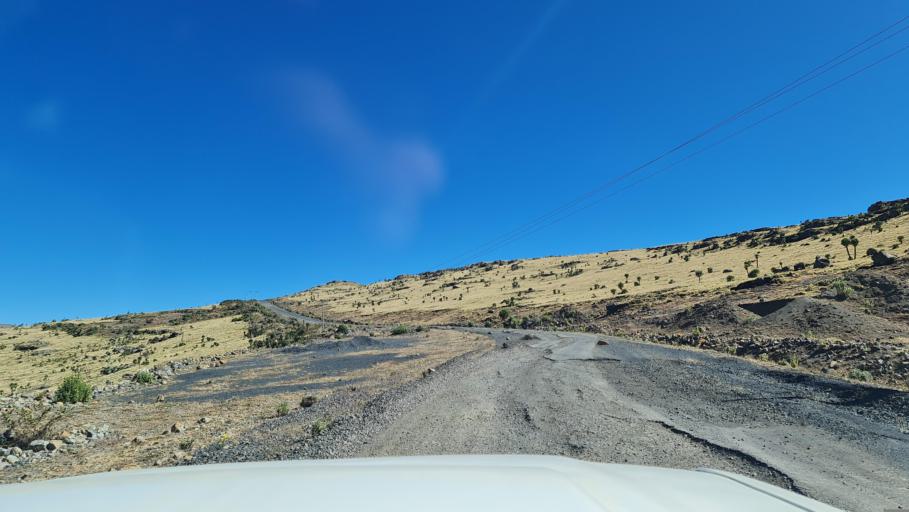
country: ET
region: Amhara
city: Debark'
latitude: 13.1630
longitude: 38.1939
